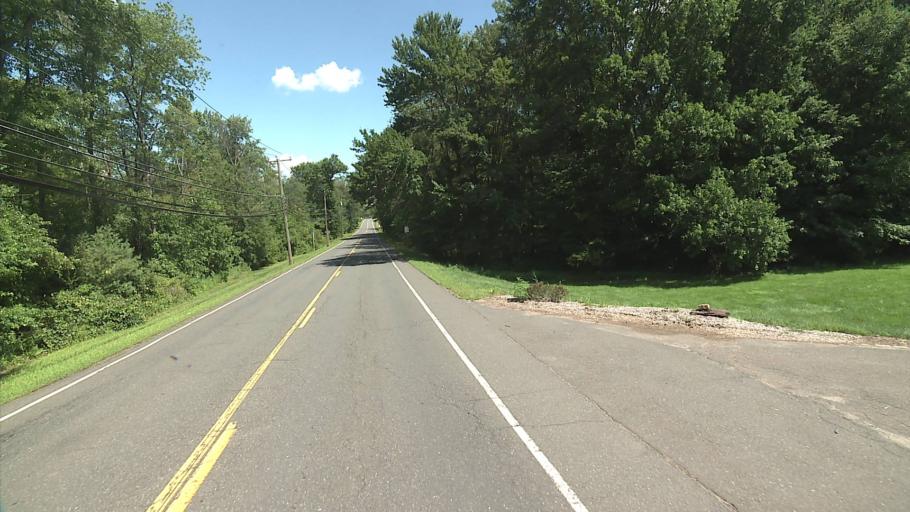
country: US
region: Connecticut
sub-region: Hartford County
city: Suffield Depot
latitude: 41.9929
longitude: -72.7104
